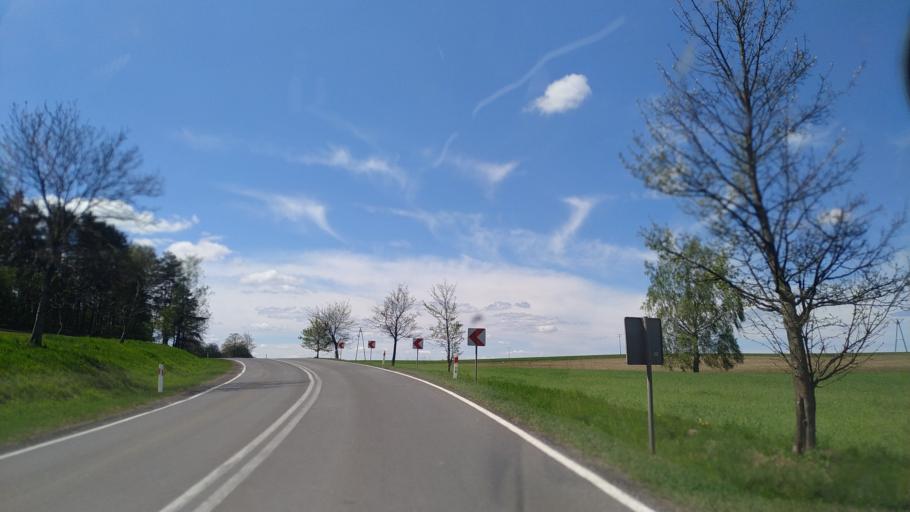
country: PL
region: Greater Poland Voivodeship
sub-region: Powiat pilski
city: Szydlowo
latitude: 53.2412
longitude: 16.6348
